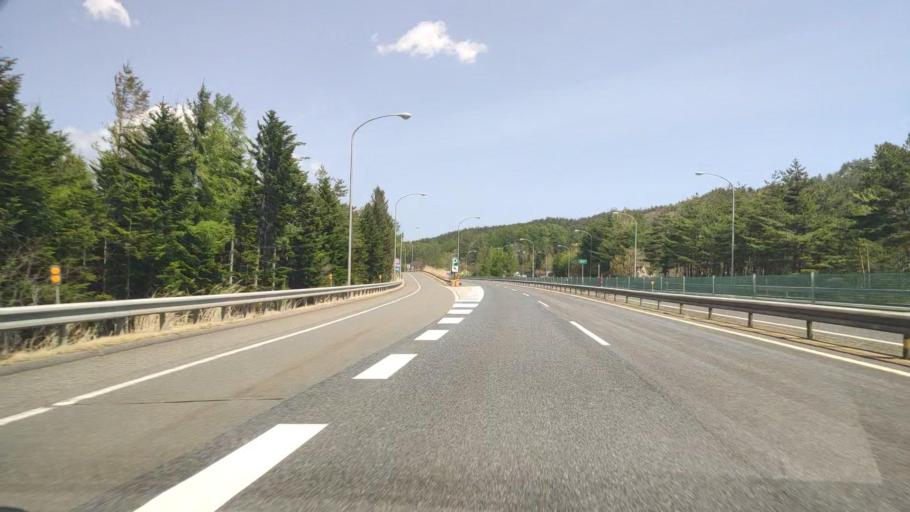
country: JP
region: Iwate
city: Ichinohe
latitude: 40.2943
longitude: 141.4220
